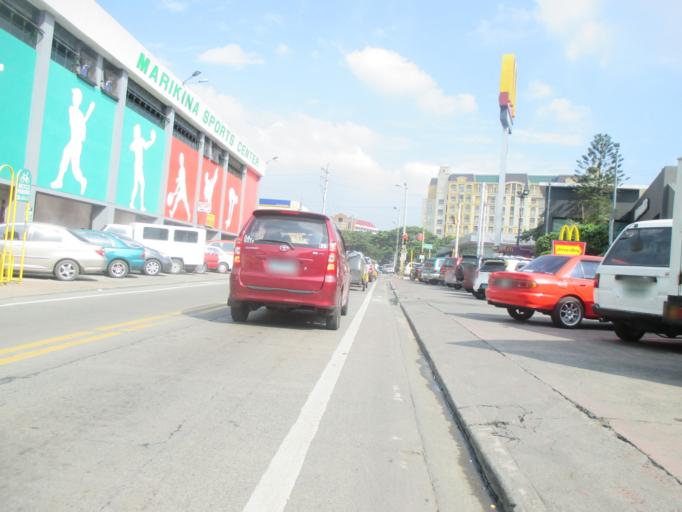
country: PH
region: Metro Manila
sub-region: Marikina
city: Calumpang
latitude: 14.6348
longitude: 121.0994
